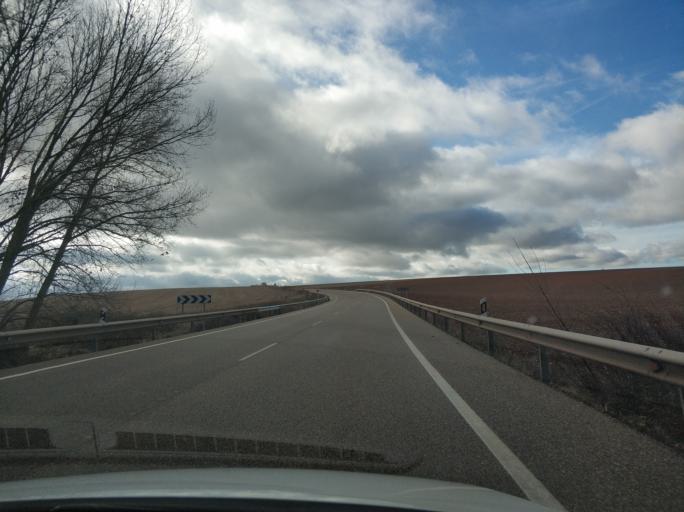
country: ES
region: Castille and Leon
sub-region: Provincia de Segovia
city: Ayllon
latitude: 41.4352
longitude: -3.3582
